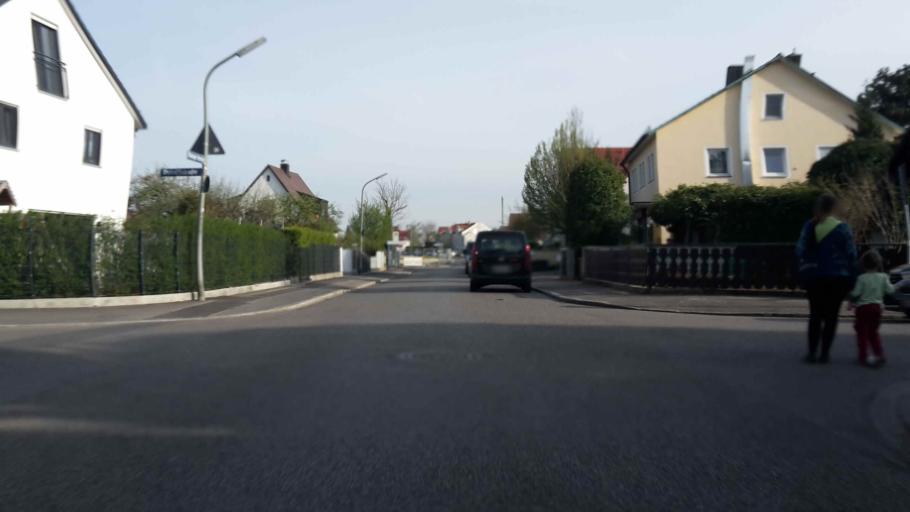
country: DE
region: Bavaria
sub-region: Upper Bavaria
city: Karlsfeld
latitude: 48.1834
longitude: 11.4469
